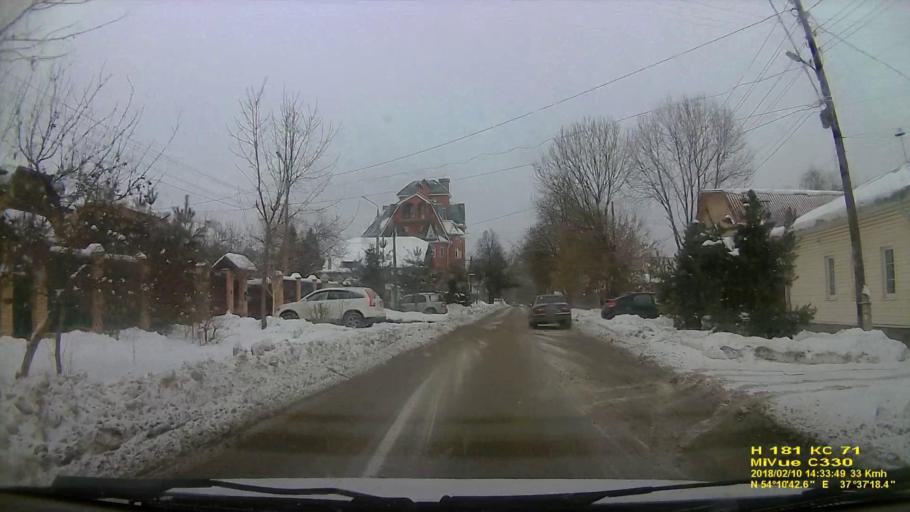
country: RU
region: Tula
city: Tula
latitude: 54.1785
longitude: 37.6218
